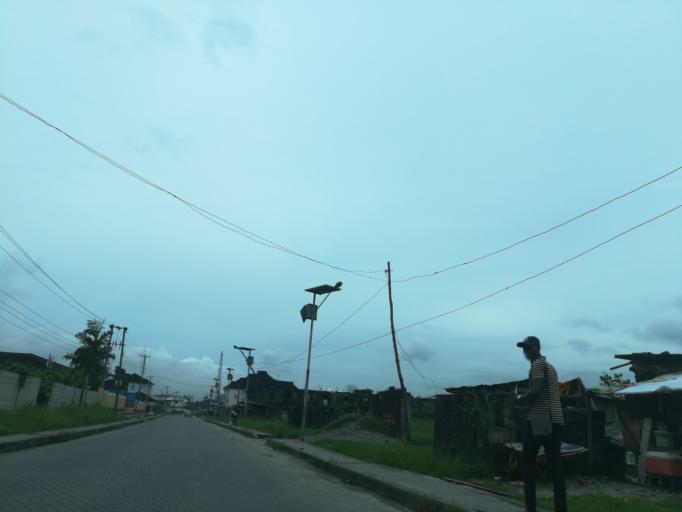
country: NG
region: Rivers
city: Port Harcourt
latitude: 4.8198
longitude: 6.9904
